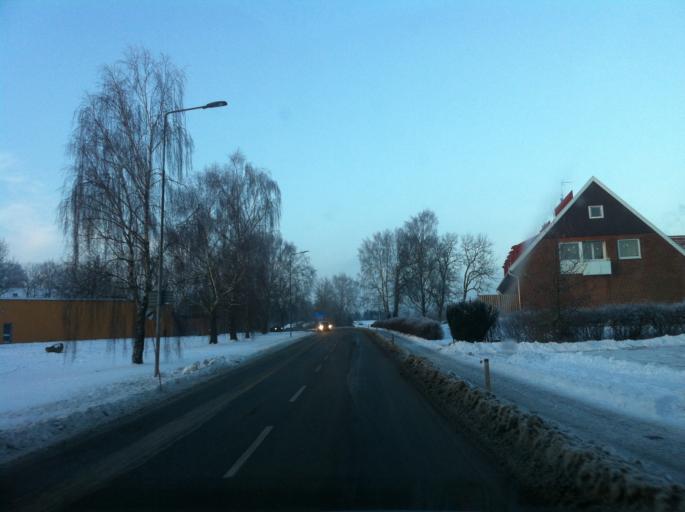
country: SE
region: Skane
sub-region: Svalovs Kommun
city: Kagerod
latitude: 55.9916
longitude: 13.0877
